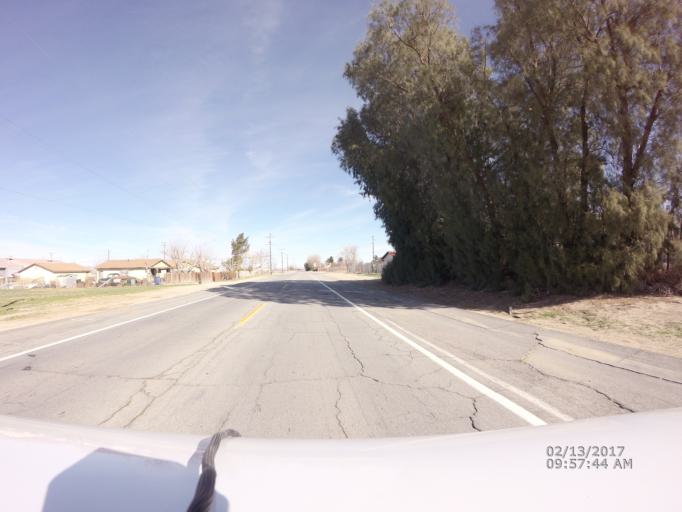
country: US
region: California
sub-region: Los Angeles County
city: Littlerock
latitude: 34.5349
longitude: -117.9748
